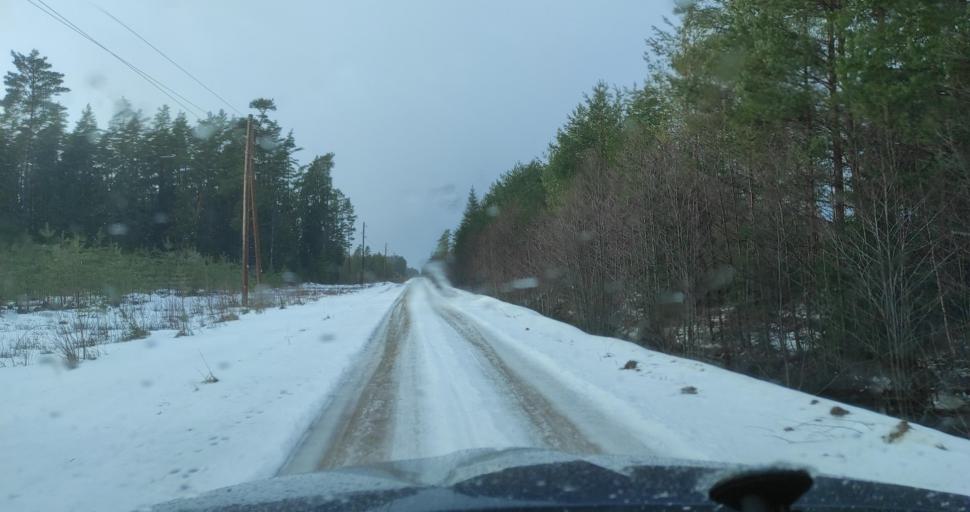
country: LV
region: Dundaga
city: Dundaga
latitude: 57.3809
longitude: 22.1561
